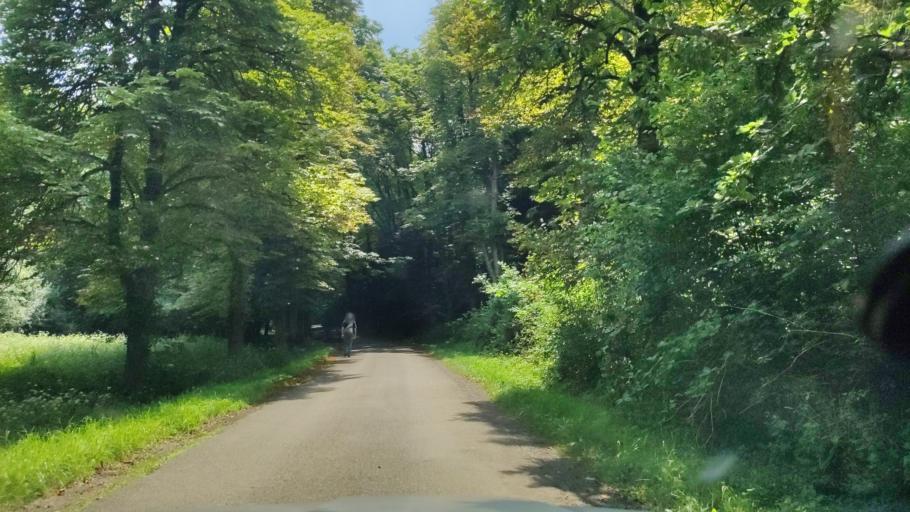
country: HU
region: Heves
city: Parad
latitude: 47.9036
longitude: 20.0553
